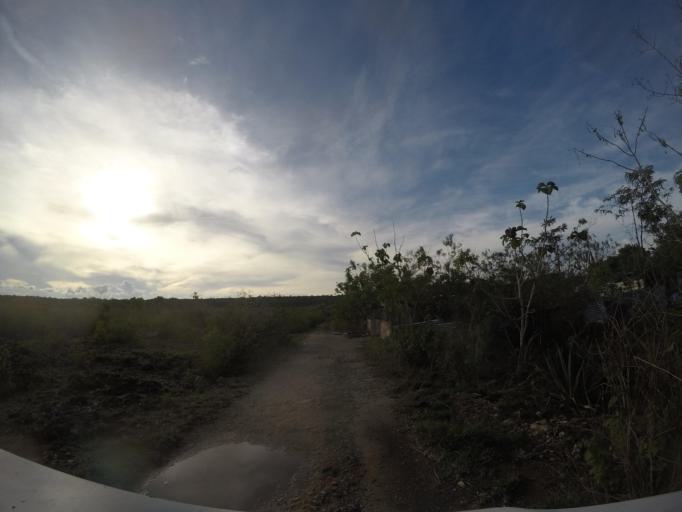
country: TL
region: Baucau
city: Baucau
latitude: -8.4879
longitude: 126.4486
